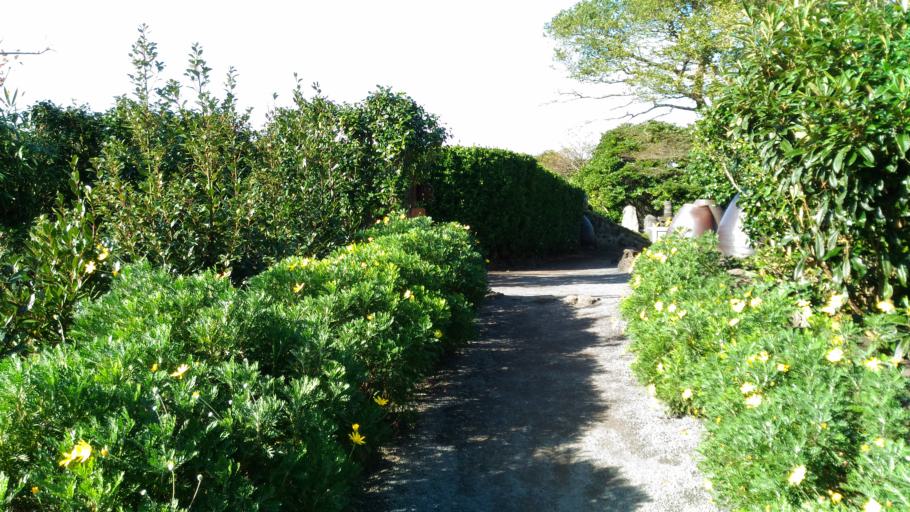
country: KR
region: Jeju-do
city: Seogwipo
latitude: 33.3225
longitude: 126.8401
